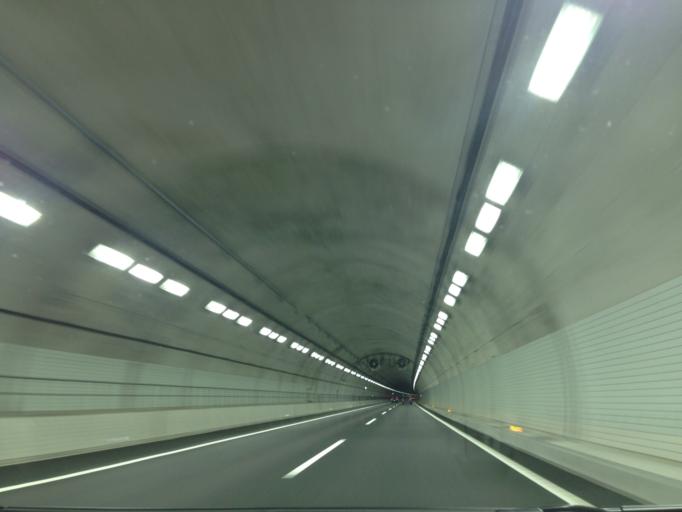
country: JP
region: Aichi
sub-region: Tokai-shi
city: Toyokawa
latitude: 34.8844
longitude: 137.4072
